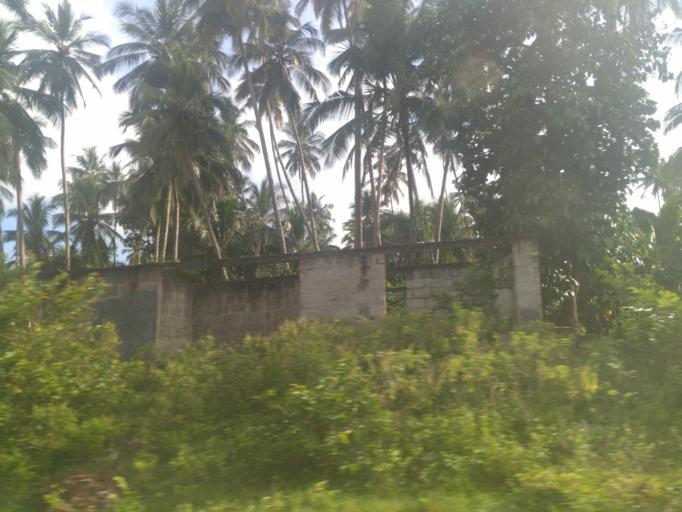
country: TZ
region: Zanzibar Central/South
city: Koani
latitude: -6.1104
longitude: 39.2998
